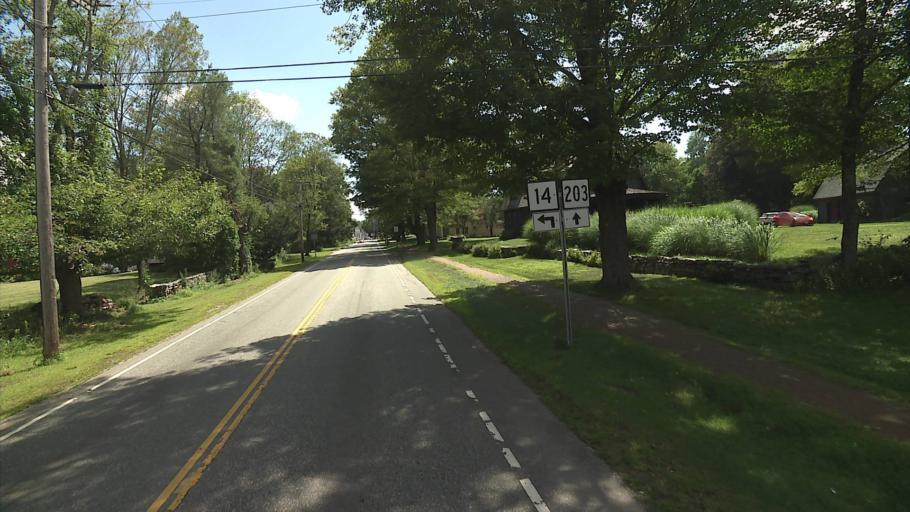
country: US
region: Connecticut
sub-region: Windham County
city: Windham
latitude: 41.7014
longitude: -72.1599
